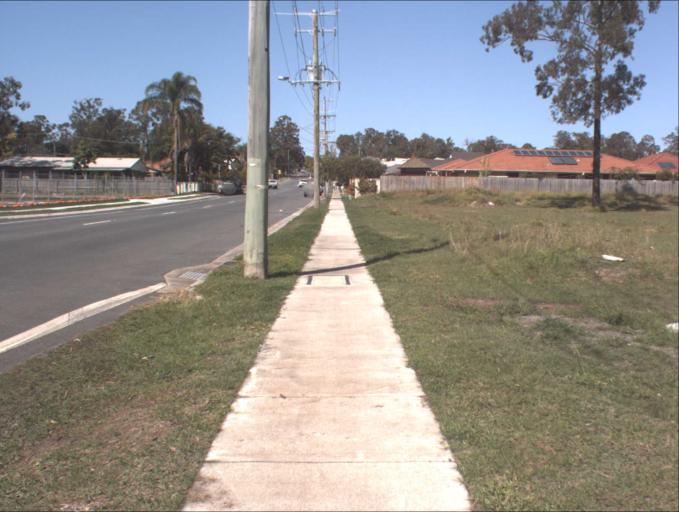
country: AU
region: Queensland
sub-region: Logan
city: Logan City
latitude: -27.6725
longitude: 153.0945
